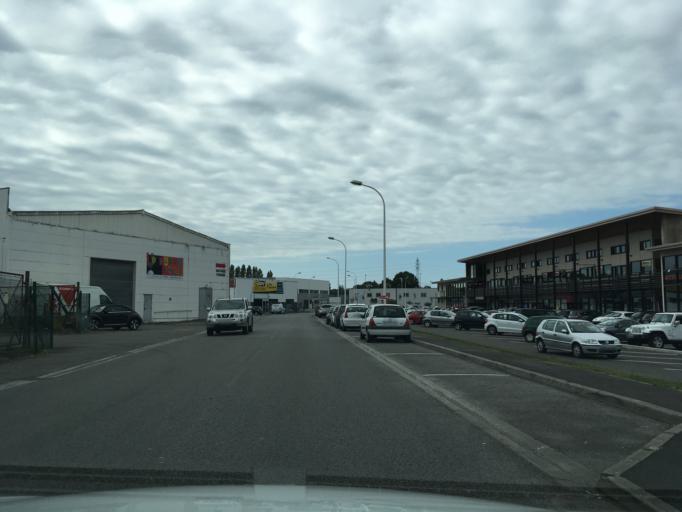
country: FR
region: Aquitaine
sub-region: Departement des Pyrenees-Atlantiques
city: Bayonne
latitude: 43.4928
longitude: -1.4921
